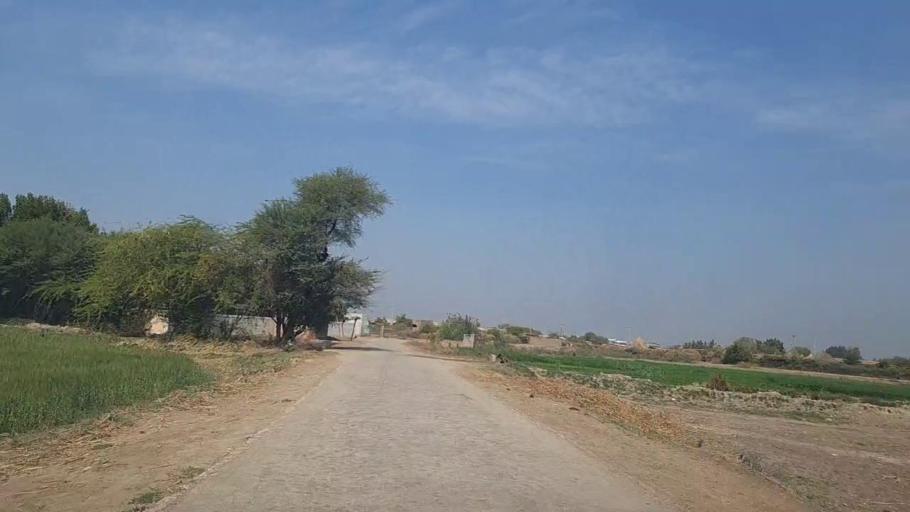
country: PK
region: Sindh
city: Mirpur Khas
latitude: 25.4998
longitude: 68.9210
